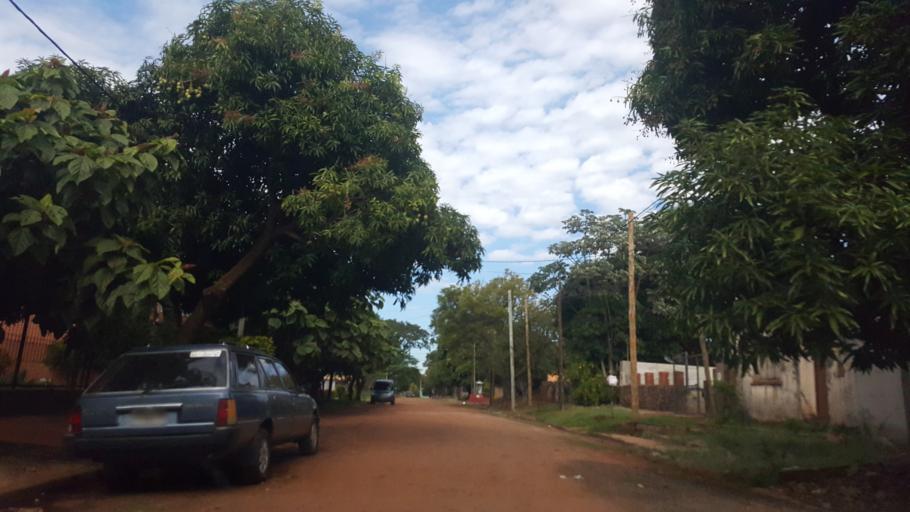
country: AR
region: Misiones
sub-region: Departamento de Capital
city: Posadas
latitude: -27.3699
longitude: -55.9186
